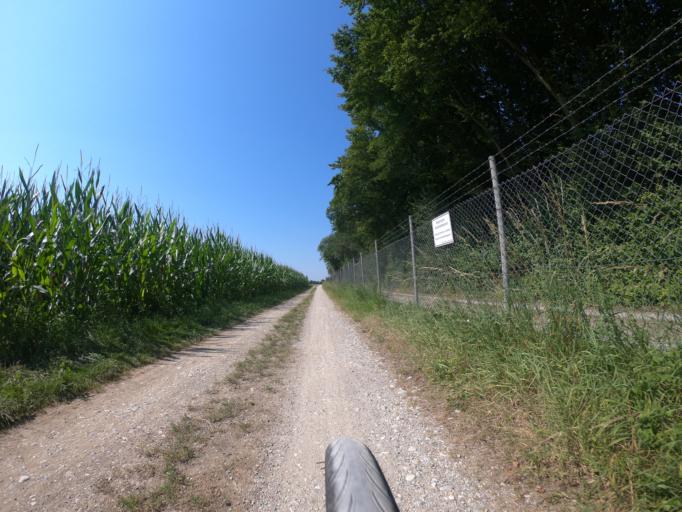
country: DE
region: Bavaria
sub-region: Upper Bavaria
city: Emmering
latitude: 48.1967
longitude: 11.2829
